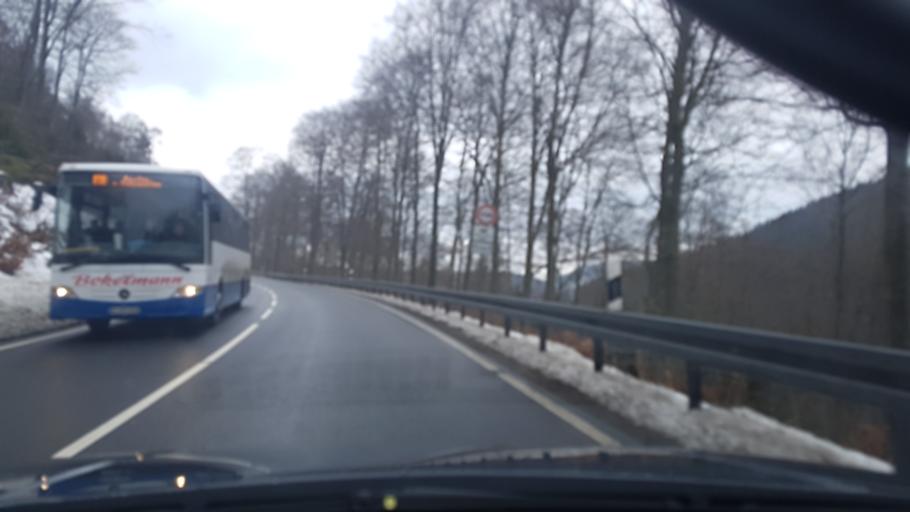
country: DE
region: Lower Saxony
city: Goslar
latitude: 51.8686
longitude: 10.3868
